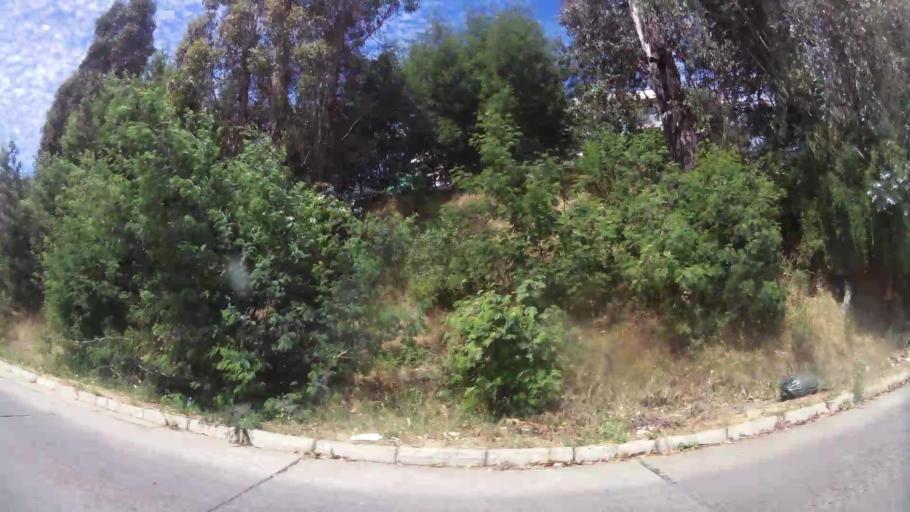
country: CL
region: Valparaiso
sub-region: Provincia de Valparaiso
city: Vina del Mar
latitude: -33.0556
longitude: -71.5826
